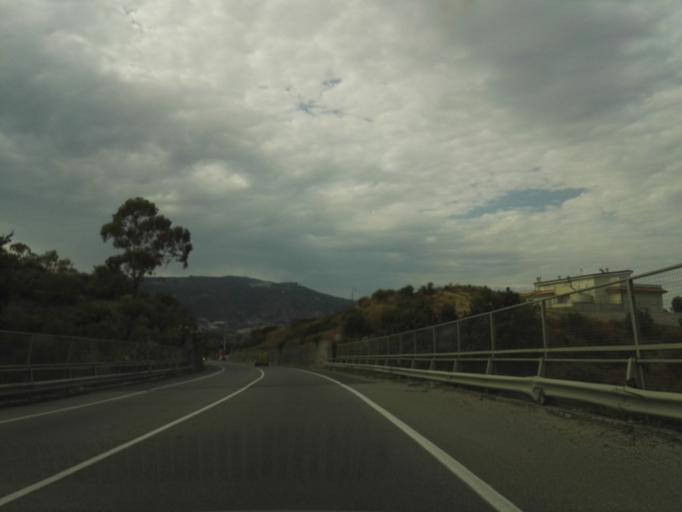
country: IT
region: Calabria
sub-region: Provincia di Catanzaro
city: Soverato Superiore
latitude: 38.6977
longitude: 16.5375
